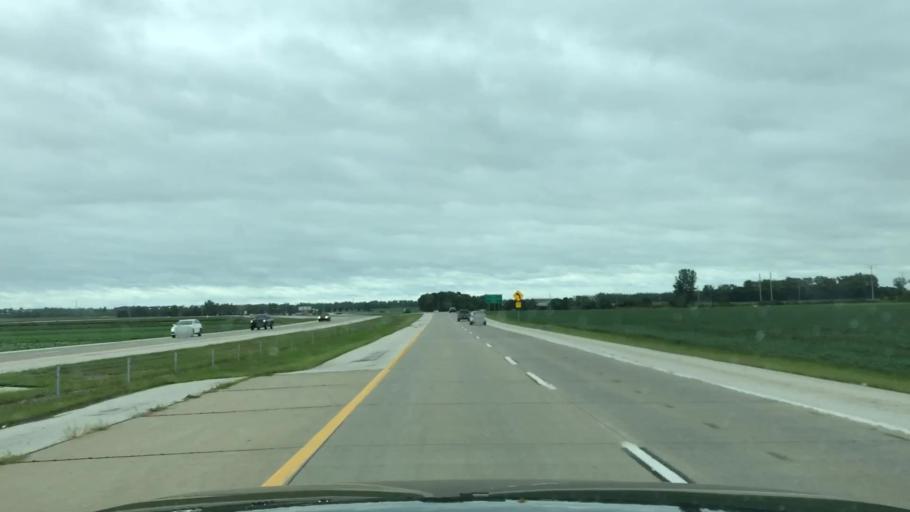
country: US
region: Missouri
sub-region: Saint Charles County
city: Saint Charles
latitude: 38.7185
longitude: -90.4985
